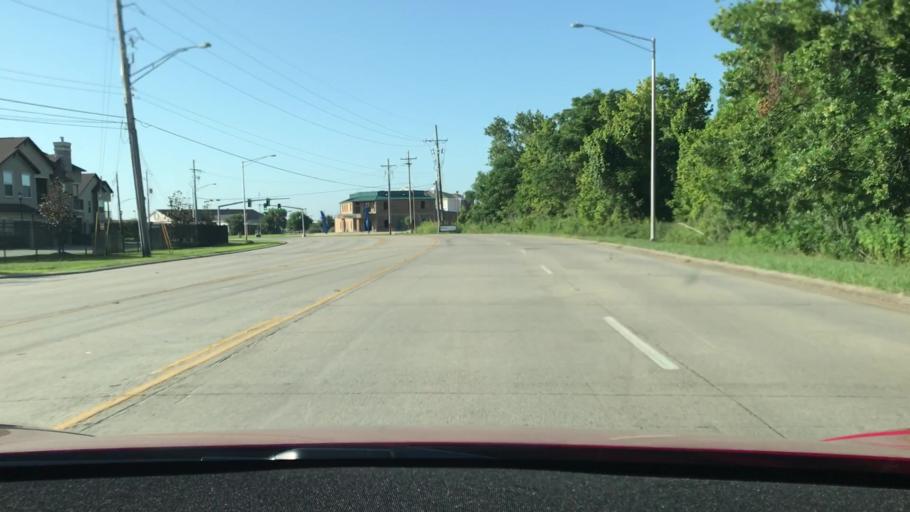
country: US
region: Louisiana
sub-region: Bossier Parish
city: Bossier City
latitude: 32.4273
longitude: -93.7250
